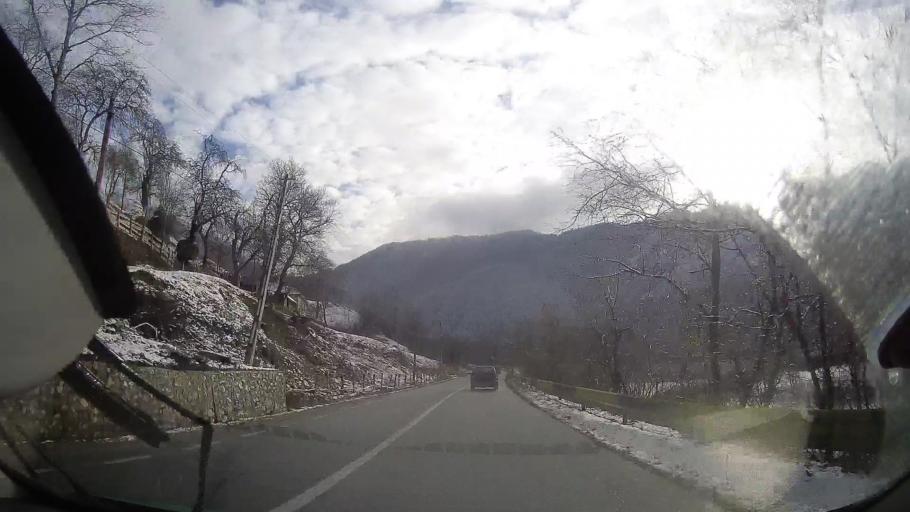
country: RO
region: Alba
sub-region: Oras Baia de Aries
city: Baia de Aries
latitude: 46.4005
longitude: 23.3094
